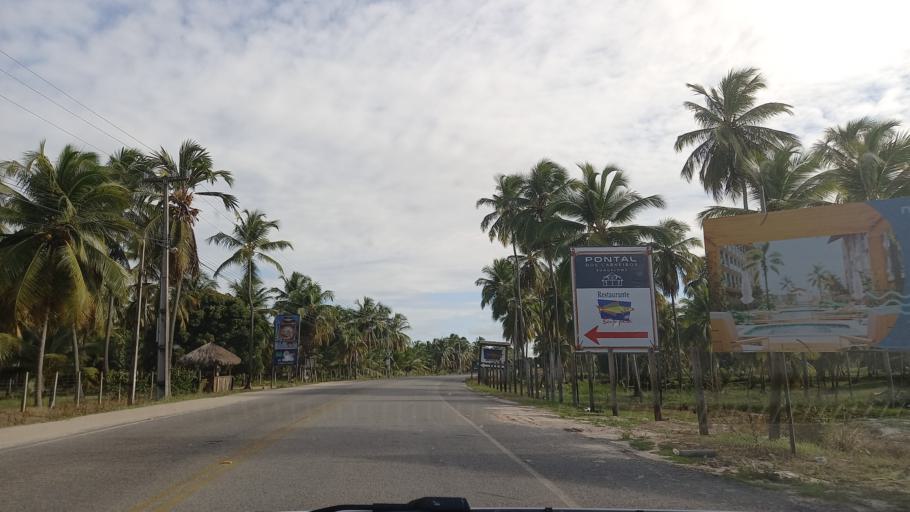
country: BR
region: Pernambuco
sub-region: Tamandare
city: Tamandare
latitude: -8.7066
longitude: -35.0871
